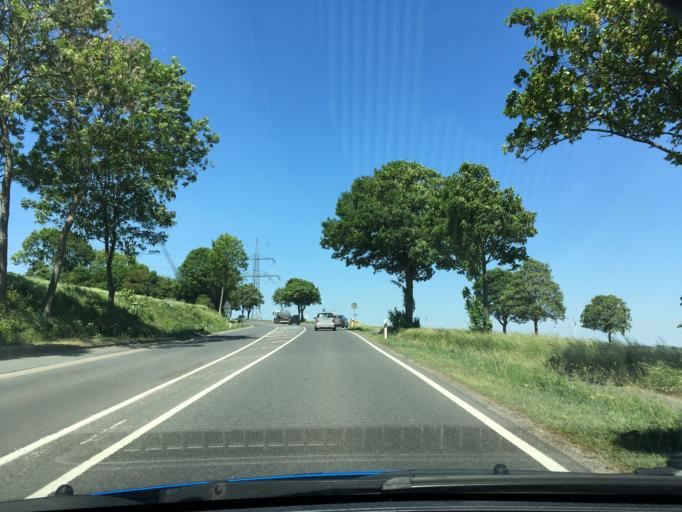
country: DE
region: Lower Saxony
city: Beckedorf
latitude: 52.3335
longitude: 9.3332
